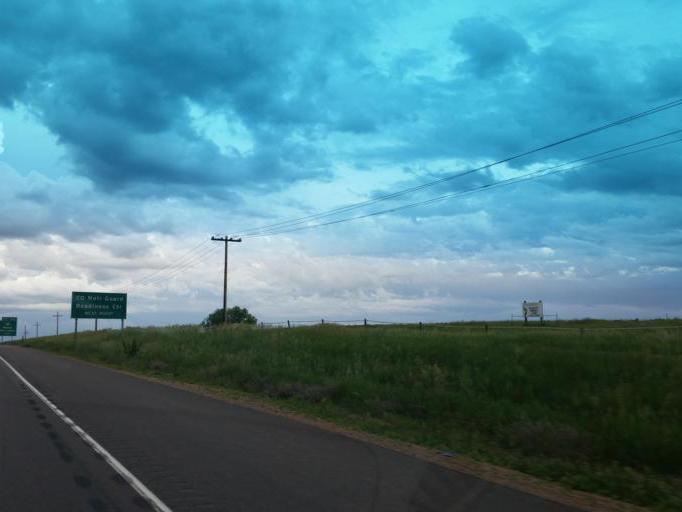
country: US
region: Colorado
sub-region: Weld County
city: Windsor
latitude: 40.4989
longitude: -104.9919
